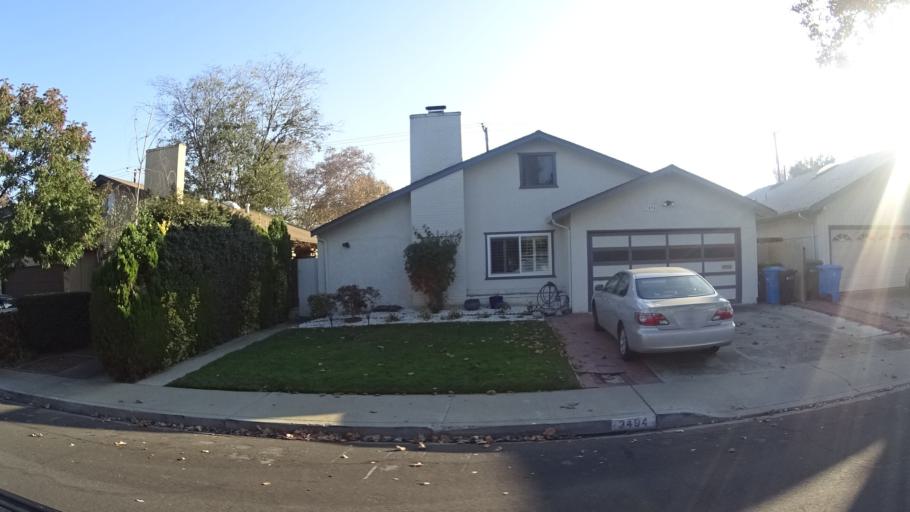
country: US
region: California
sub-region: Santa Clara County
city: Santa Clara
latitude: 37.3443
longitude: -121.9923
